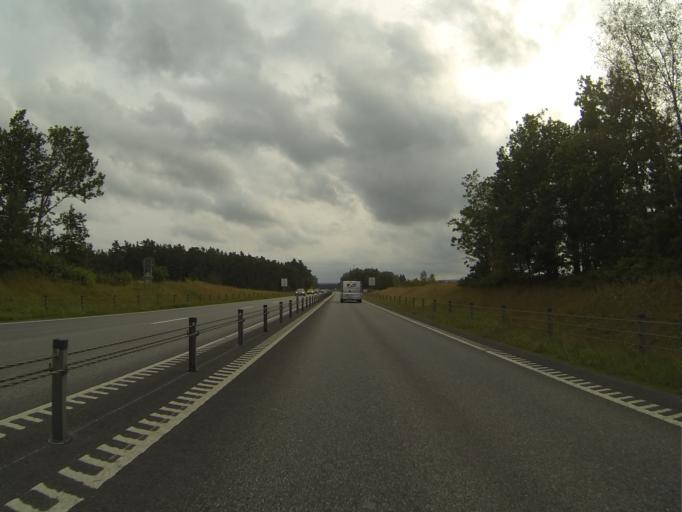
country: SE
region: Skane
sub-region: Kristianstads Kommun
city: Norra Asum
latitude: 55.9685
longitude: 14.0750
